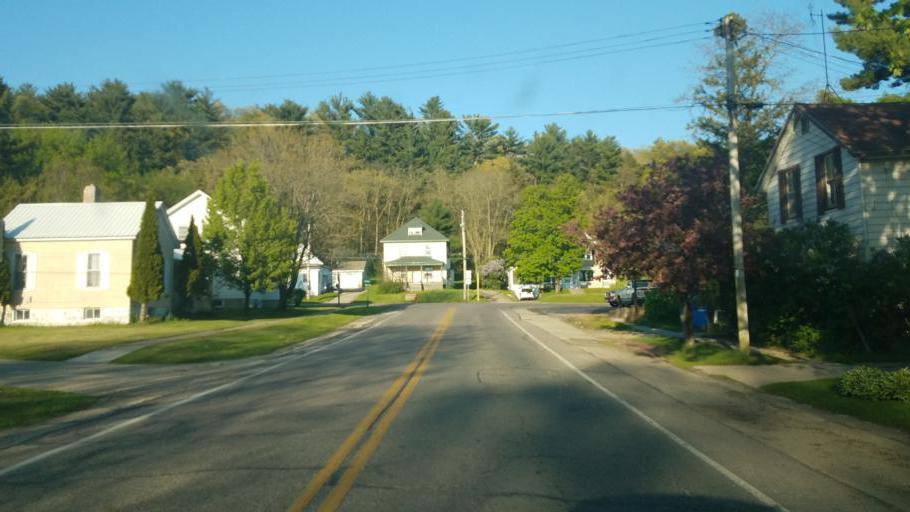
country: US
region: Wisconsin
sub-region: Juneau County
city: Elroy
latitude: 43.6517
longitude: -90.2227
